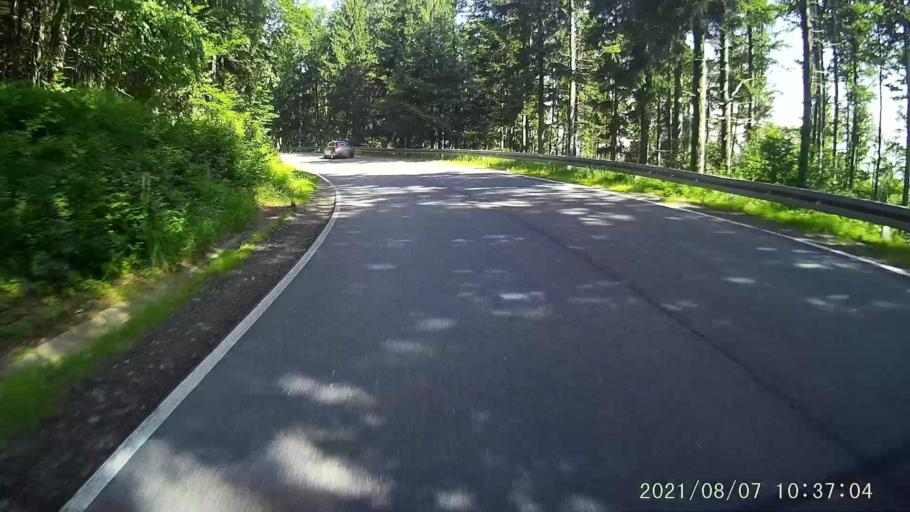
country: PL
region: Lower Silesian Voivodeship
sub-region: Powiat klodzki
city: Duszniki-Zdroj
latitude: 50.3591
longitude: 16.3758
